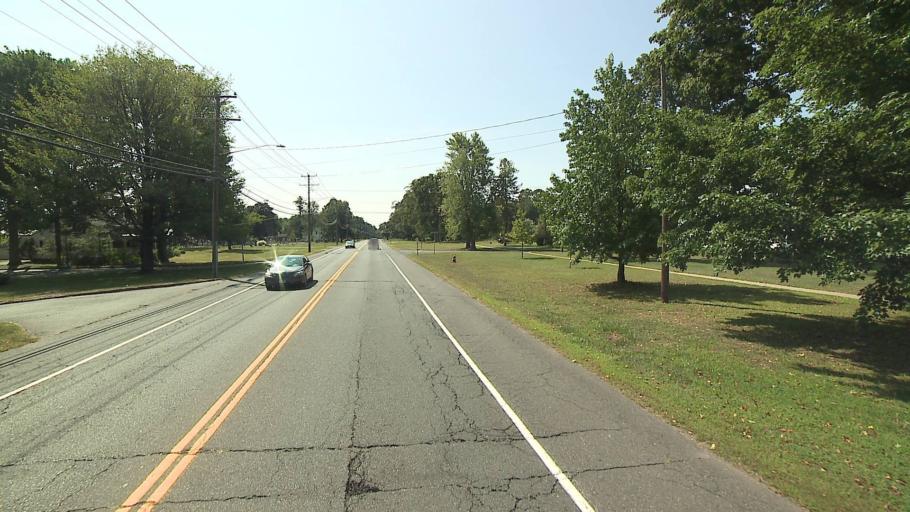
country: US
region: Connecticut
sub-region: Hartford County
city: Enfield
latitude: 41.9860
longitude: -72.5932
